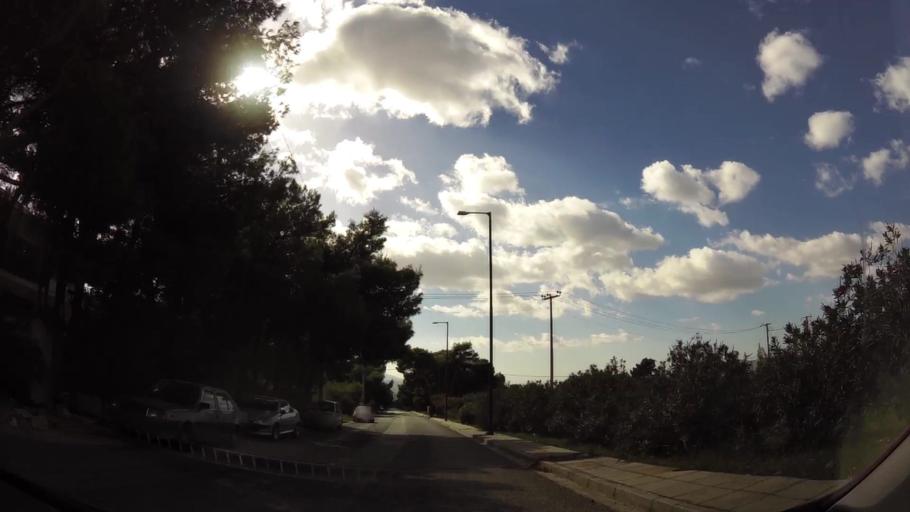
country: GR
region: Attica
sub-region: Nomarchia Anatolikis Attikis
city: Thrakomakedones
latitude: 38.1295
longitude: 23.7506
